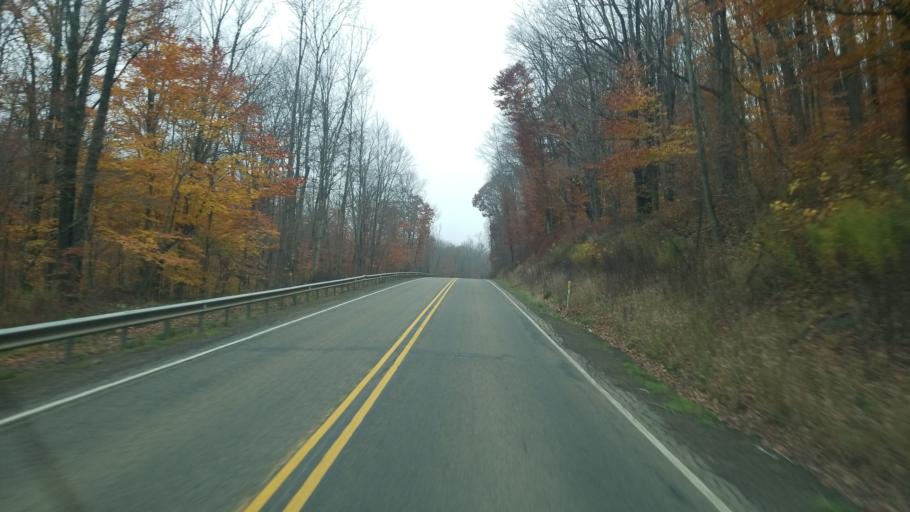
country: US
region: Pennsylvania
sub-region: McKean County
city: Smethport
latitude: 41.8092
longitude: -78.4979
